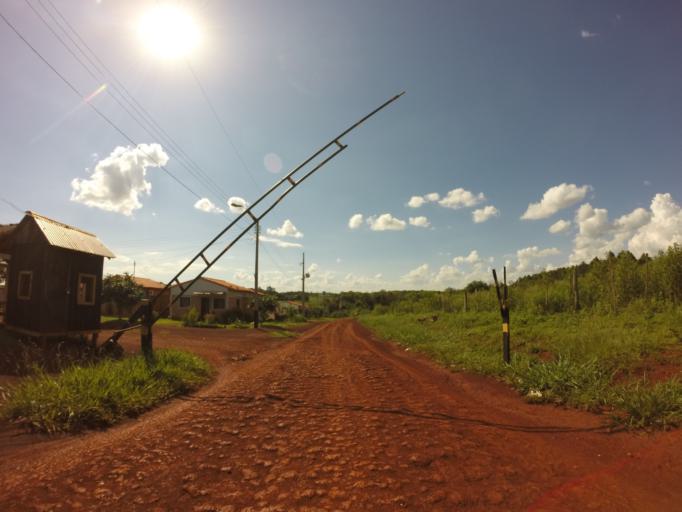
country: PY
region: Alto Parana
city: Ciudad del Este
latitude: -25.3724
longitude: -54.6673
